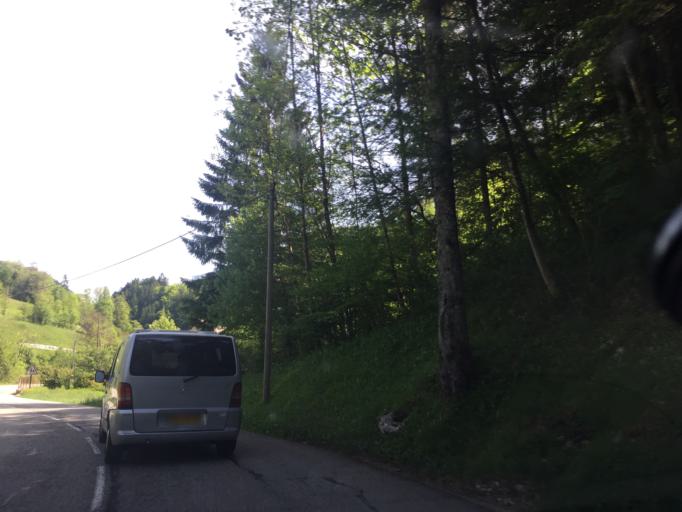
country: FR
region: Rhone-Alpes
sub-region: Departement de l'Isere
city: Saint-Vincent-de-Mercuze
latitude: 45.4244
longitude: 5.8639
